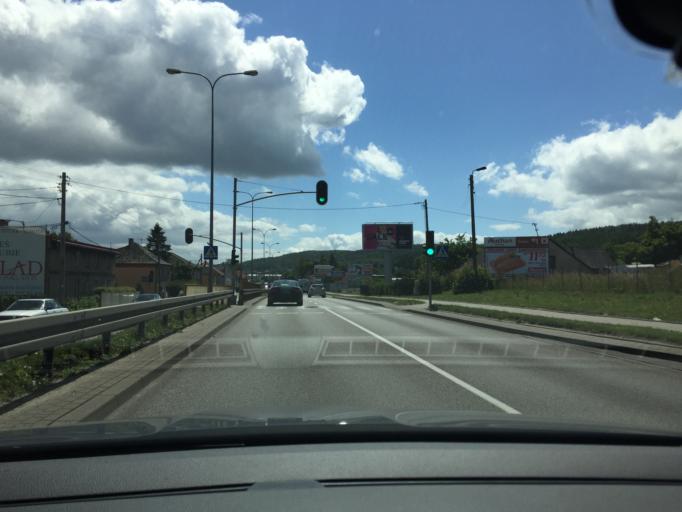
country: PL
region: Pomeranian Voivodeship
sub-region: Powiat wejherowski
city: Reda
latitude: 54.5882
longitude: 18.3609
